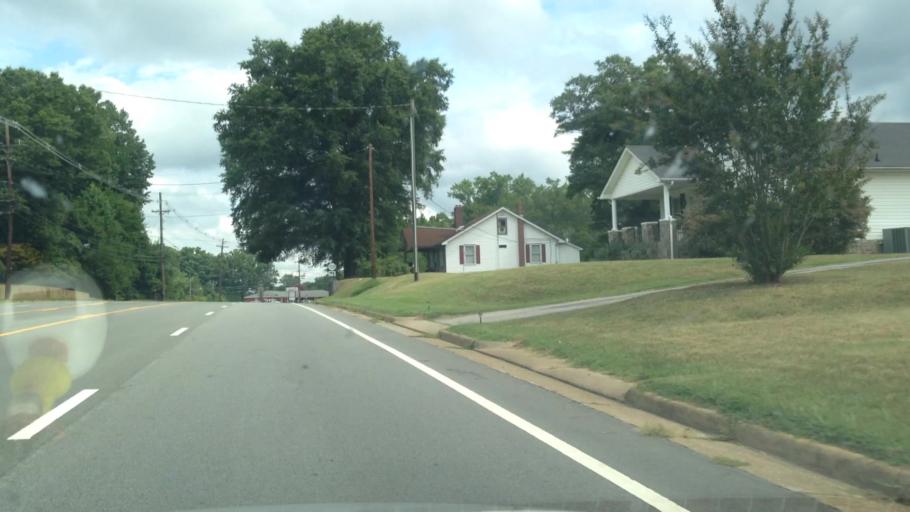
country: US
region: Virginia
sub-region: Pittsylvania County
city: Mount Hermon
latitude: 36.6755
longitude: -79.3744
